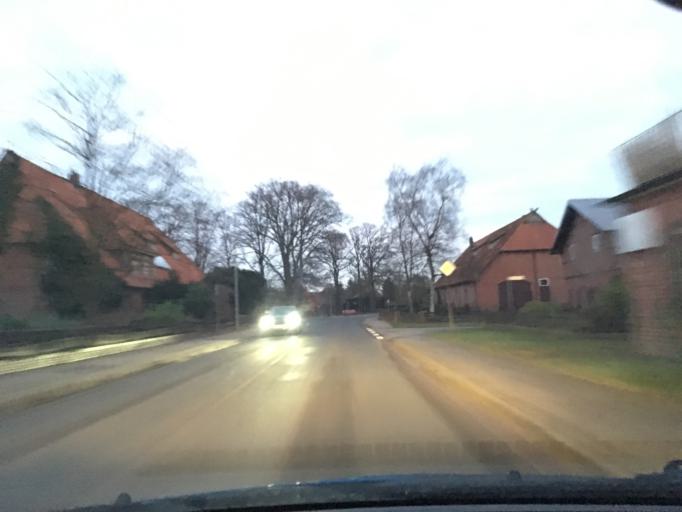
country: DE
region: Lower Saxony
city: Brietlingen
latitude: 53.3331
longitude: 10.4376
